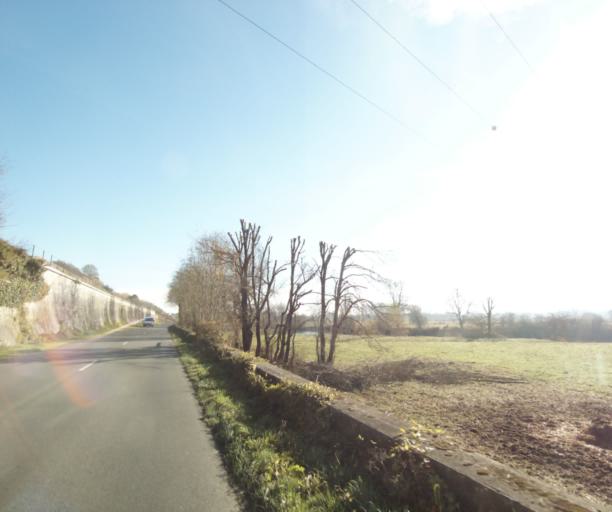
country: FR
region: Poitou-Charentes
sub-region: Departement de la Charente-Maritime
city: Les Gonds
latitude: 45.7306
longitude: -0.5981
